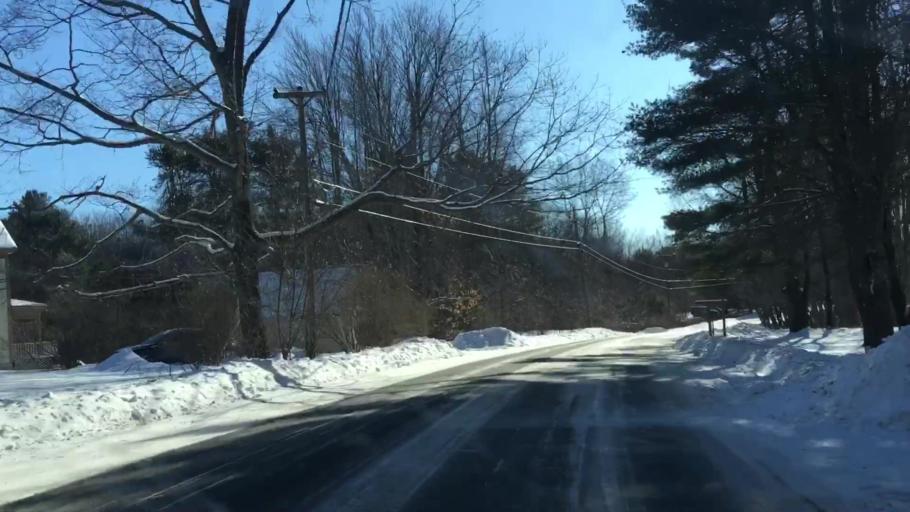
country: US
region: Maine
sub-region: Cumberland County
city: Brunswick
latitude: 43.8982
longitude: -69.9988
